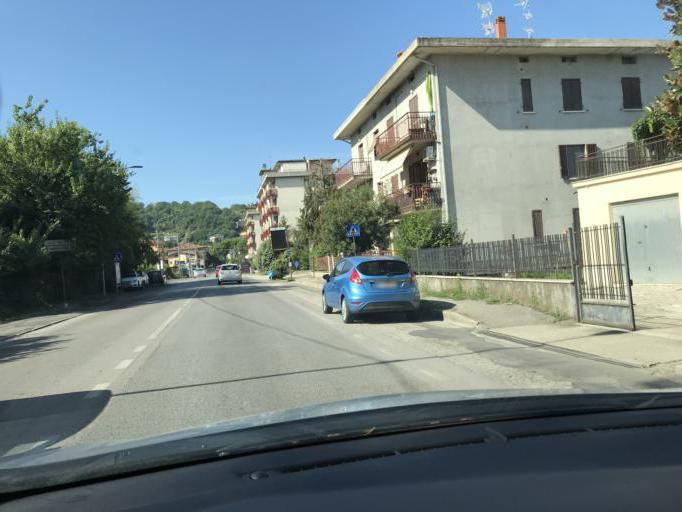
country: IT
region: Umbria
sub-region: Provincia di Perugia
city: Ponte Felcino
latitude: 43.1115
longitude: 12.4496
